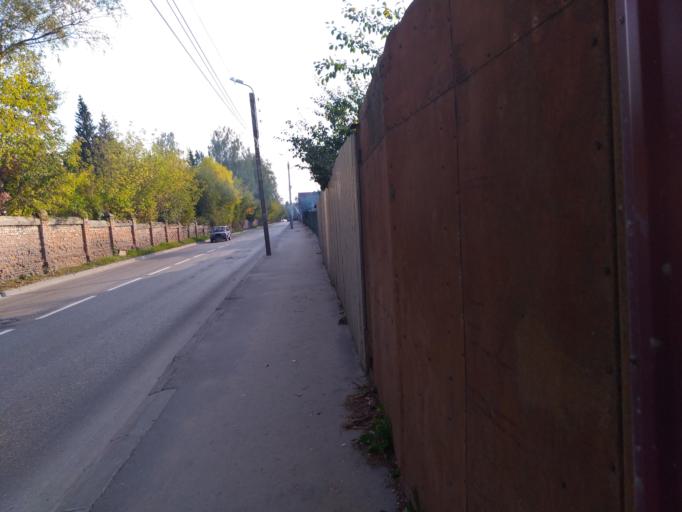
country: RU
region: Kaluga
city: Kaluga
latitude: 54.5264
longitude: 36.2541
